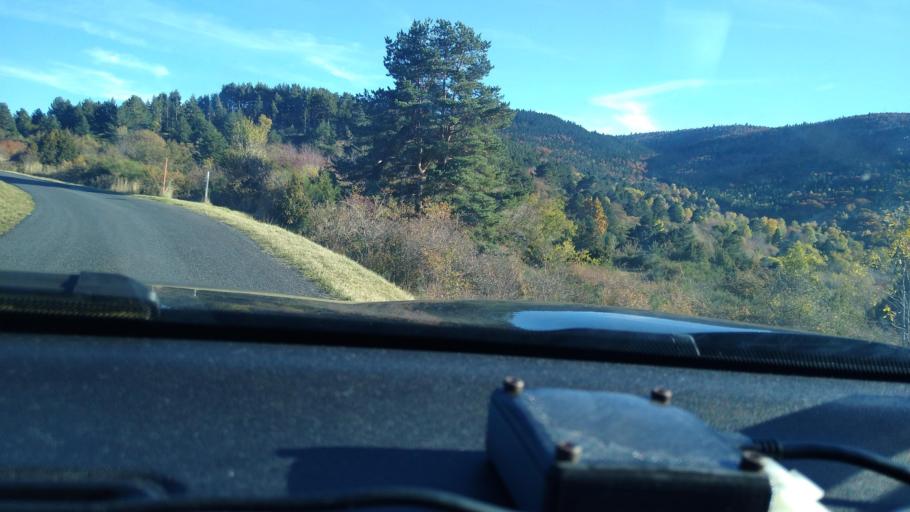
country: FR
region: Languedoc-Roussillon
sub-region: Departement de l'Aude
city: Quillan
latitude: 42.7378
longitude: 2.1493
